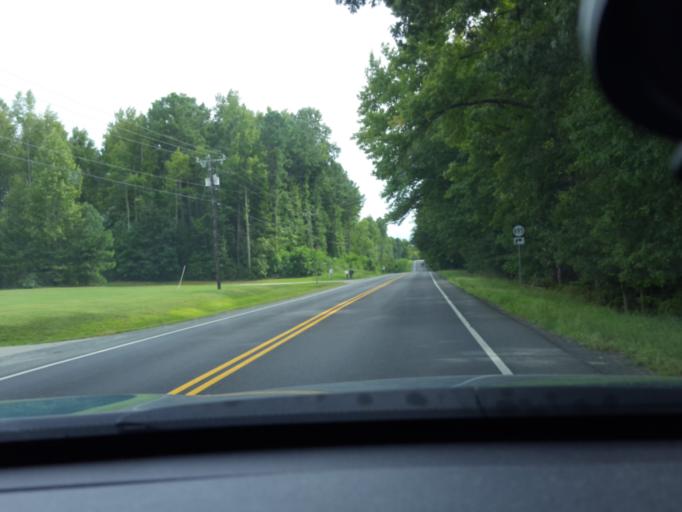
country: US
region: Virginia
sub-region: Hanover County
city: Hanover
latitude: 37.7430
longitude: -77.3585
